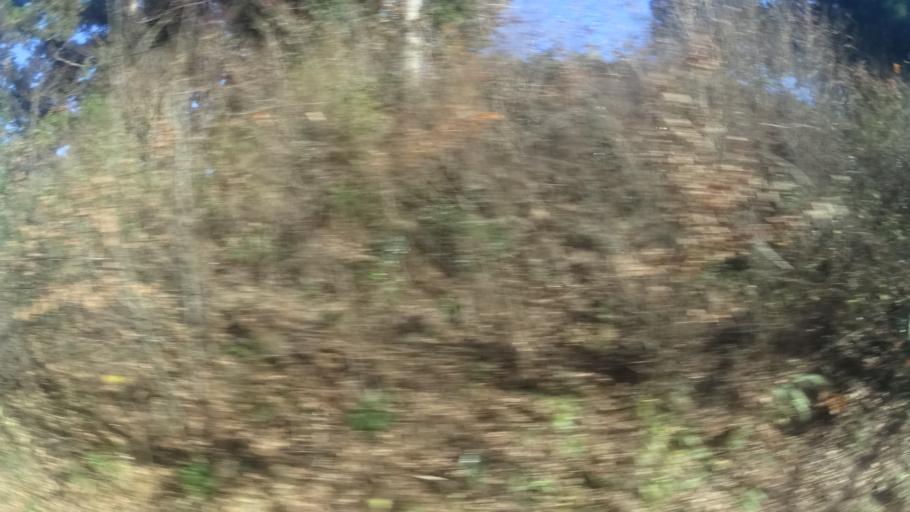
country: JP
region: Fukushima
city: Namie
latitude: 37.6908
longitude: 140.9734
